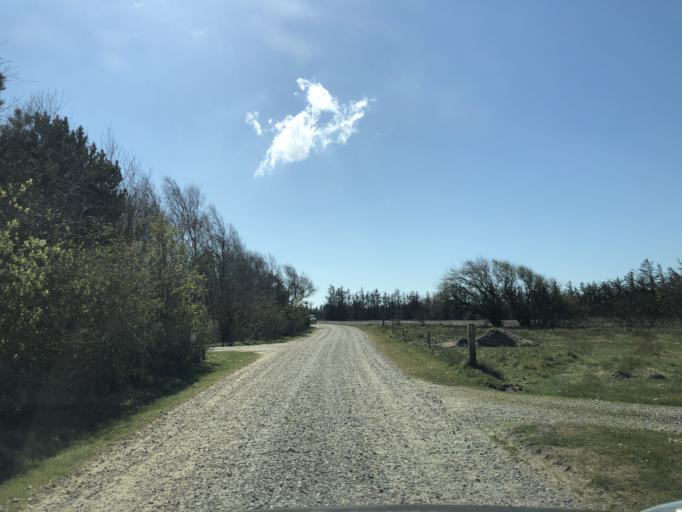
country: DK
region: Central Jutland
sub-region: Holstebro Kommune
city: Ulfborg
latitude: 56.3202
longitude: 8.1983
